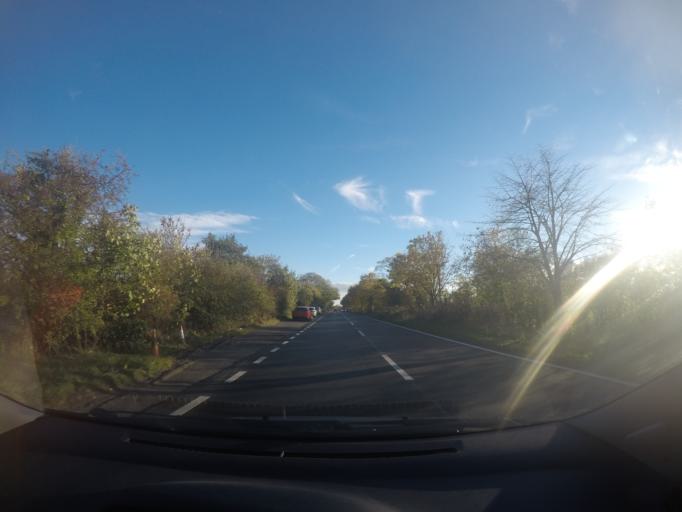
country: GB
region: England
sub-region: City of York
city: York
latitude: 53.9834
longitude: -1.0833
